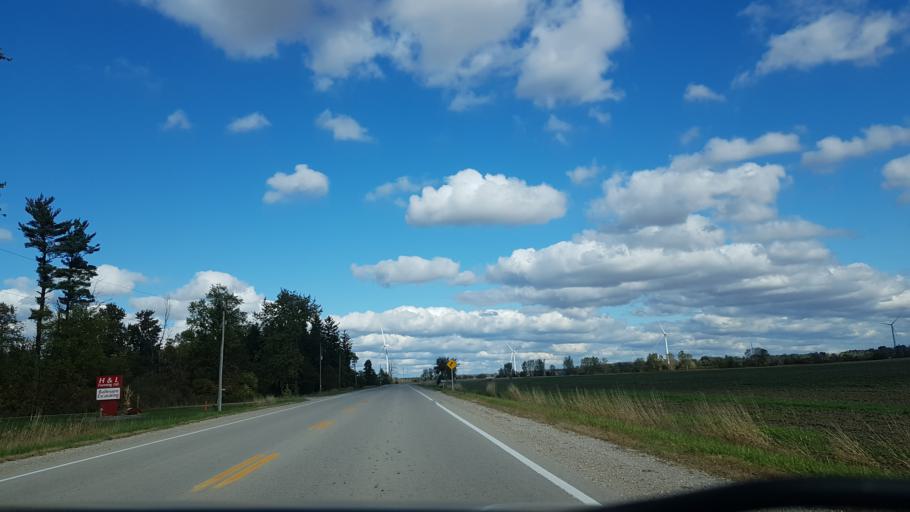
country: CA
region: Ontario
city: Lambton Shores
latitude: 43.2373
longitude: -81.7868
